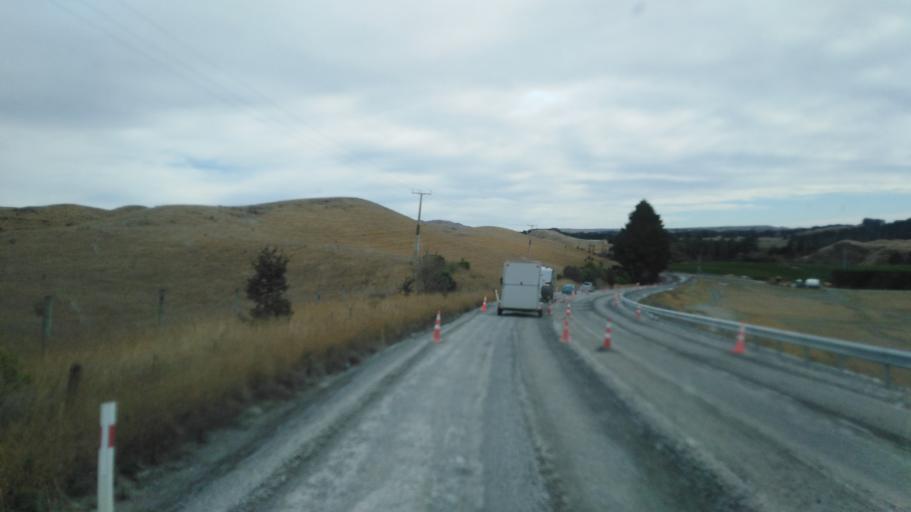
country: NZ
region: Marlborough
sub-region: Marlborough District
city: Blenheim
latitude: -41.8715
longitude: 174.1180
